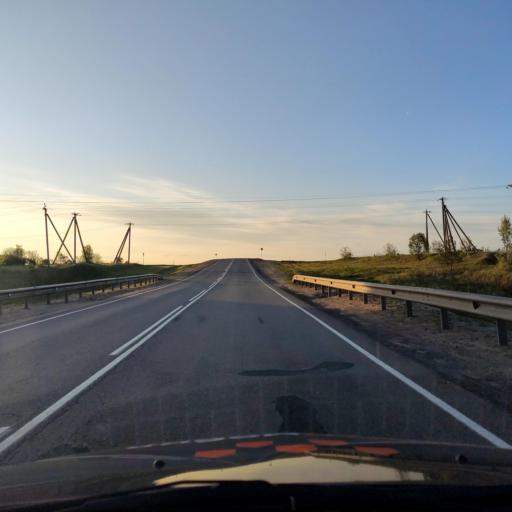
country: RU
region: Orjol
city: Livny
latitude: 52.4486
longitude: 37.5137
